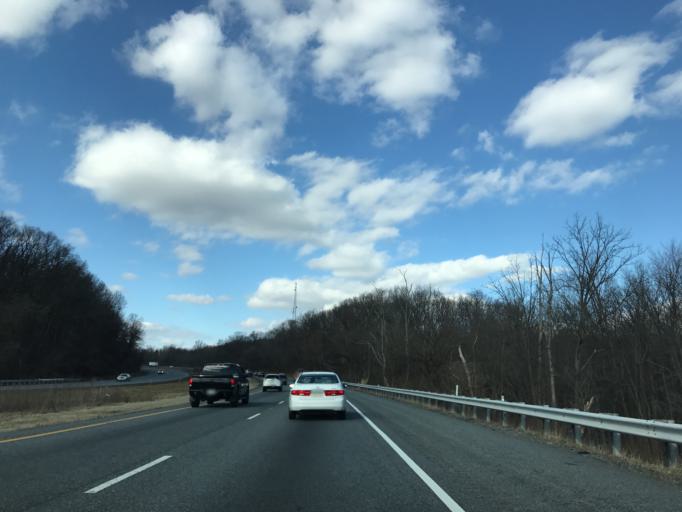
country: US
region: Pennsylvania
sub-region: York County
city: New Freedom
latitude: 39.6979
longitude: -76.6411
